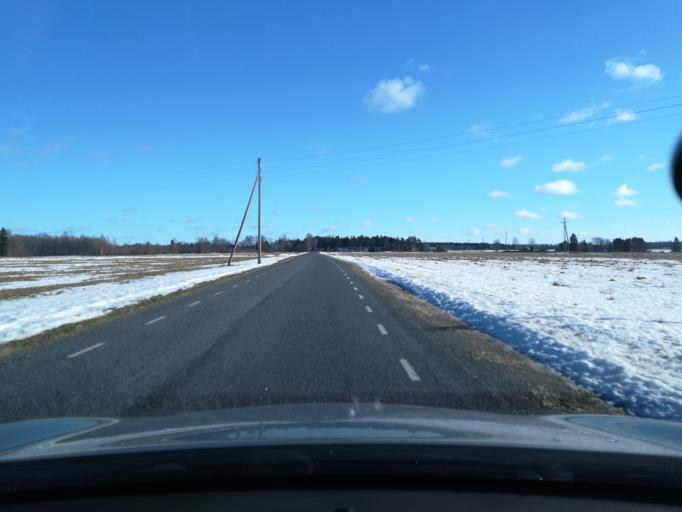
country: EE
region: Raplamaa
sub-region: Kohila vald
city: Kohila
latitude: 59.2299
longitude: 24.7373
